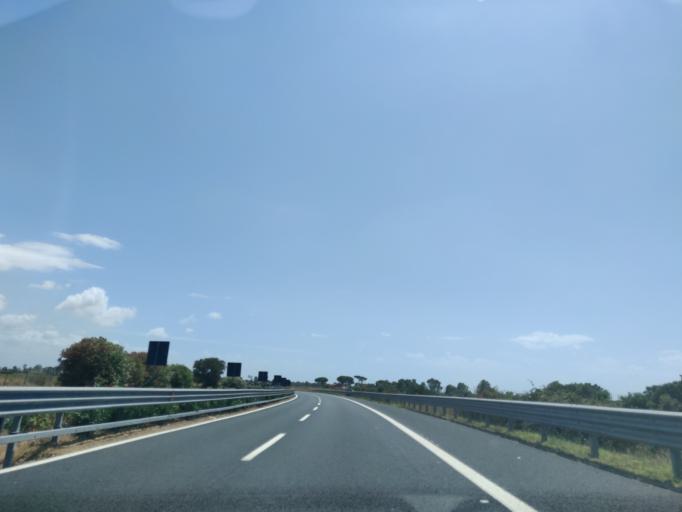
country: IT
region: Latium
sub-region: Citta metropolitana di Roma Capitale
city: Maccarese
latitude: 41.8563
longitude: 12.2630
